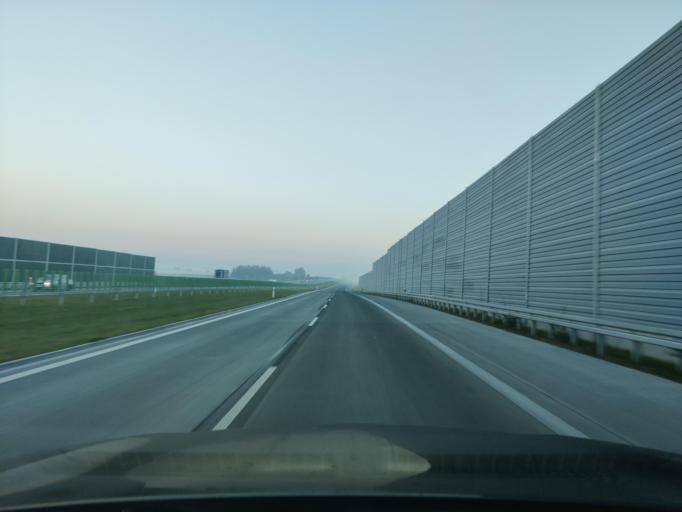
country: PL
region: Masovian Voivodeship
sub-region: Powiat plonski
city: Plonsk
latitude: 52.6600
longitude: 20.3781
